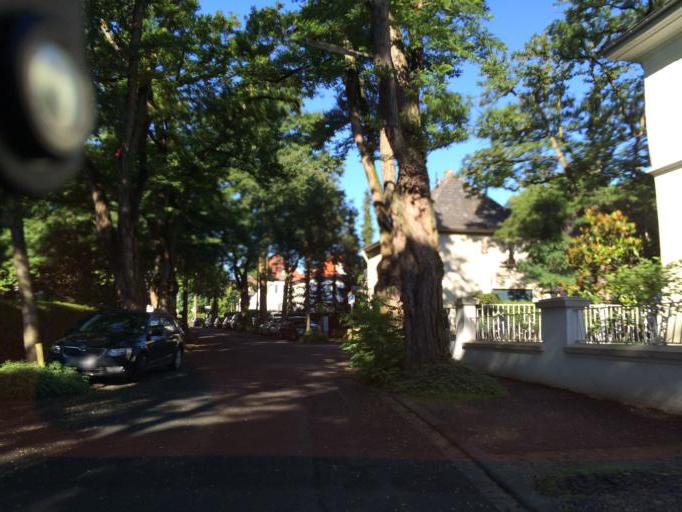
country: DE
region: North Rhine-Westphalia
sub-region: Regierungsbezirk Koln
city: Konigswinter
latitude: 50.6941
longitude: 7.1645
